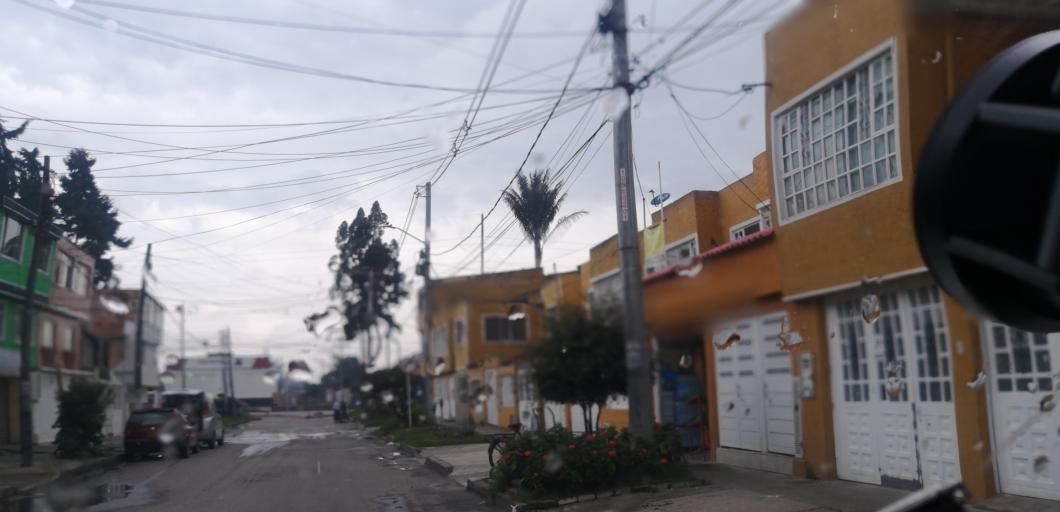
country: CO
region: Cundinamarca
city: Funza
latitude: 4.6805
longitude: -74.1542
